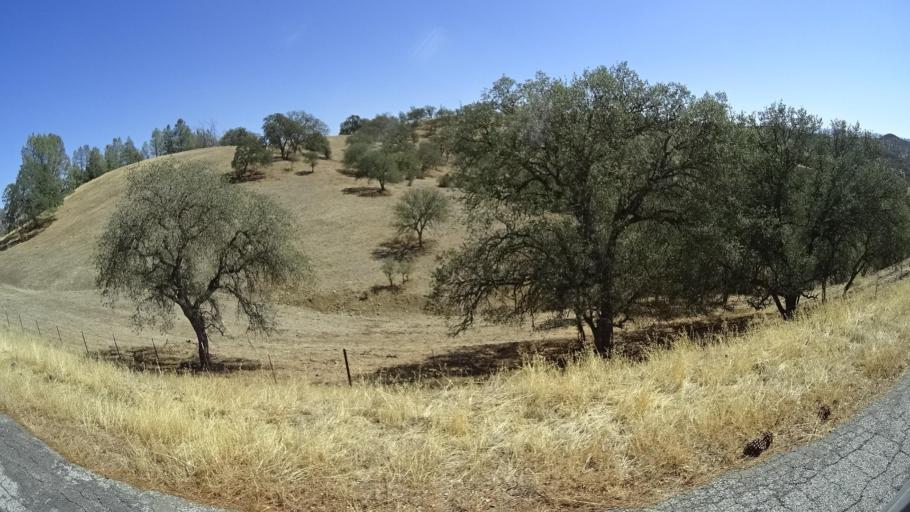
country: US
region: California
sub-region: Fresno County
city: Coalinga
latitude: 36.0636
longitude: -120.6580
